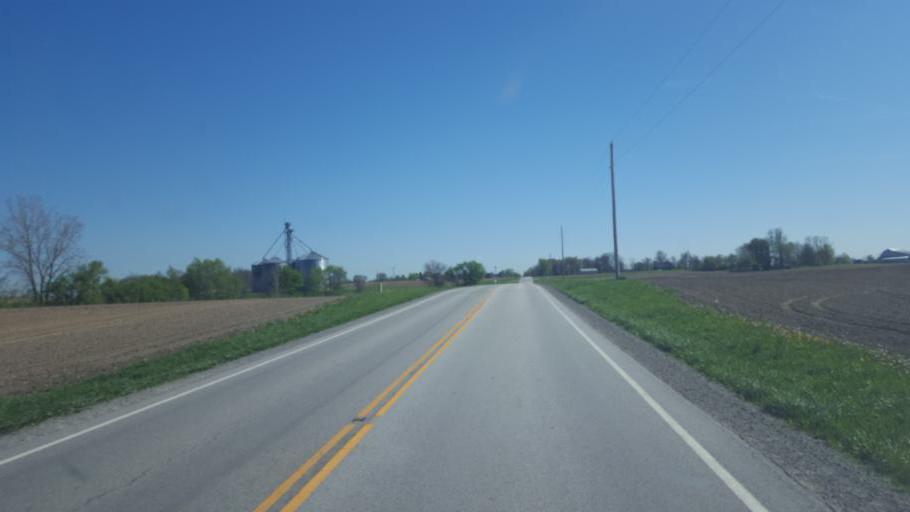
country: US
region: Ohio
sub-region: Wyandot County
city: Upper Sandusky
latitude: 40.9174
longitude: -83.2104
